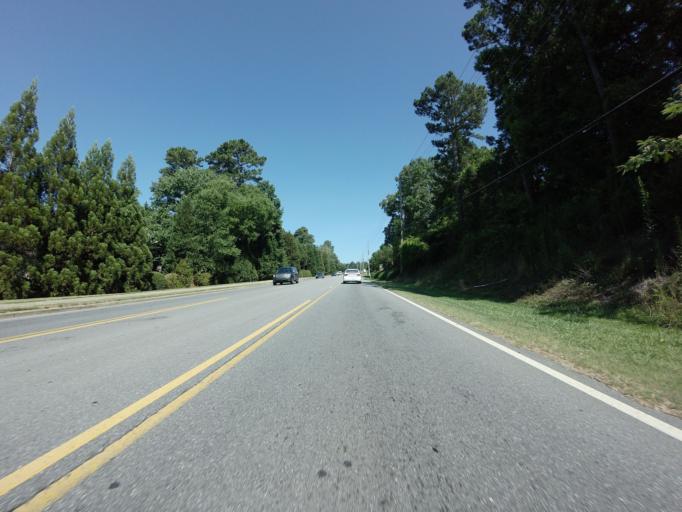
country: US
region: Georgia
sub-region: Fulton County
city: Johns Creek
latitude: 34.0884
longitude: -84.1960
